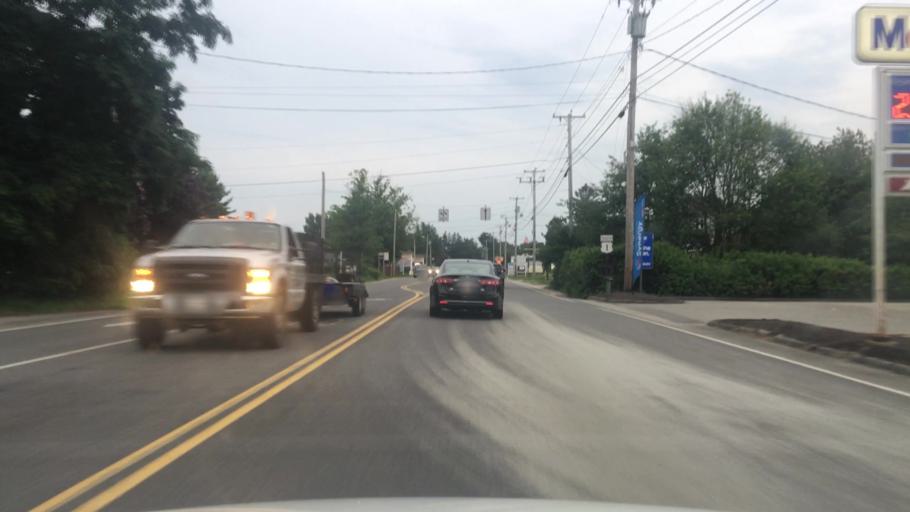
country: US
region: Maine
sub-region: York County
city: Wells Beach Station
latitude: 43.2944
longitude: -70.5889
